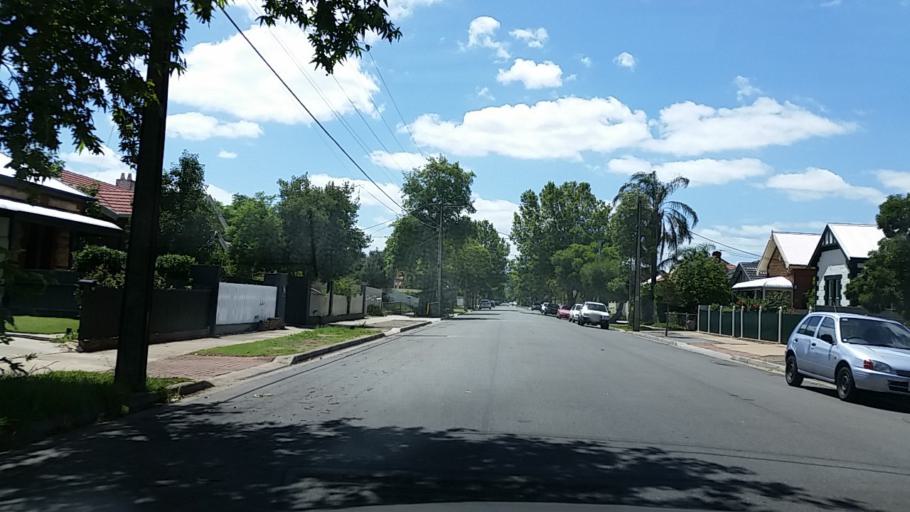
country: AU
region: South Australia
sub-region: City of West Torrens
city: Thebarton
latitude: -34.9270
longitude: 138.5618
